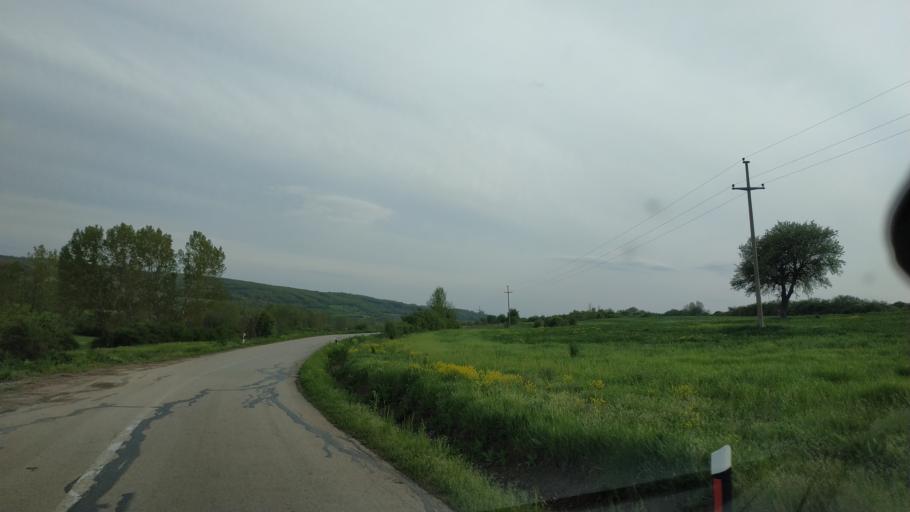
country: RS
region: Central Serbia
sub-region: Zajecarski Okrug
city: Soko Banja
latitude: 43.5152
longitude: 21.8453
